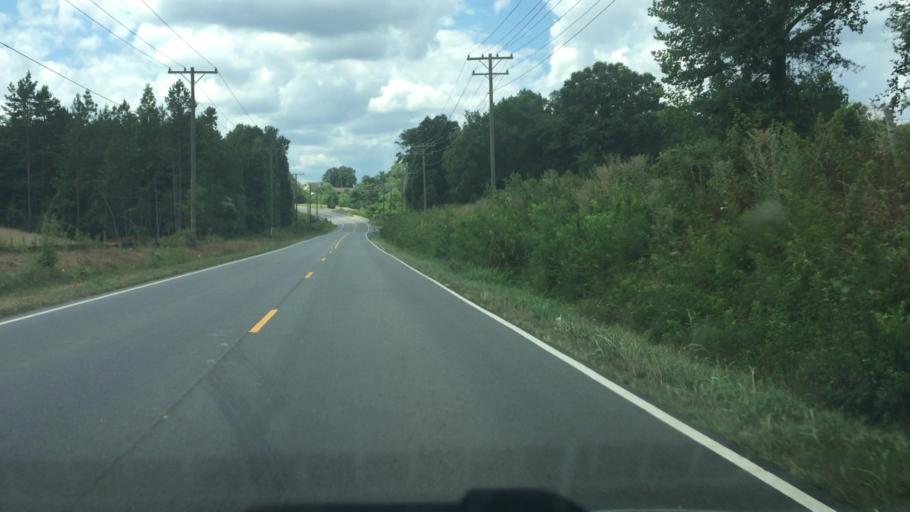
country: US
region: North Carolina
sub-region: Mecklenburg County
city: Huntersville
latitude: 35.4159
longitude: -80.7496
